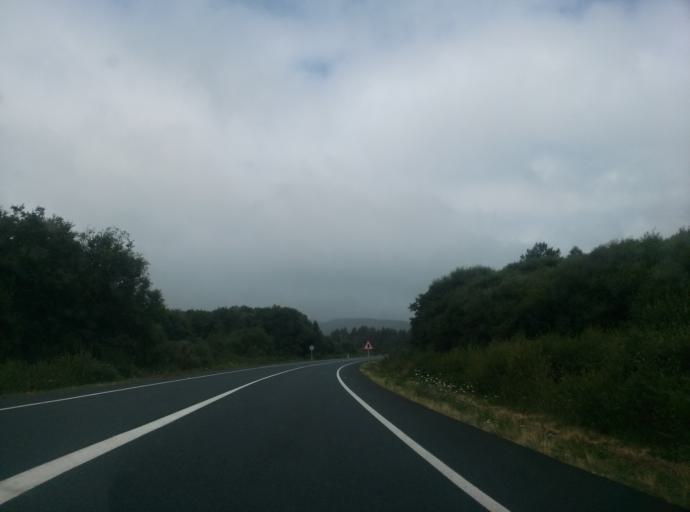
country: ES
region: Galicia
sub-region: Provincia de Lugo
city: Muras
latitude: 43.4188
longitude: -7.7651
